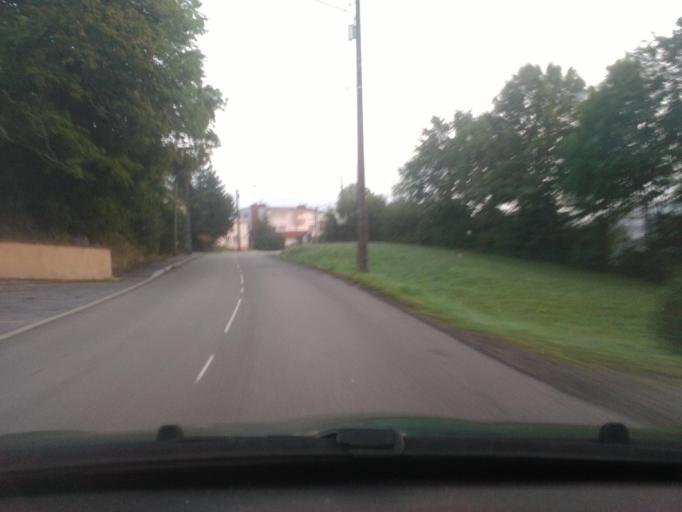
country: FR
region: Lorraine
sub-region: Departement des Vosges
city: Corcieux
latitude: 48.1697
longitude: 6.8760
